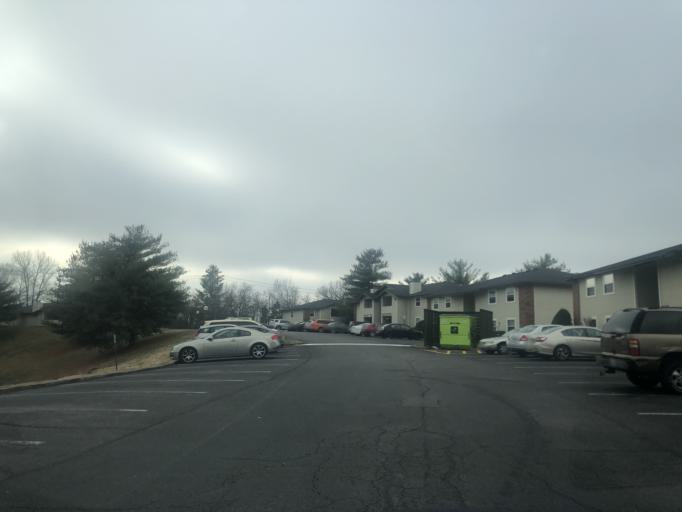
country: US
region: Tennessee
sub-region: Rutherford County
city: La Vergne
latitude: 36.0687
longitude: -86.6420
